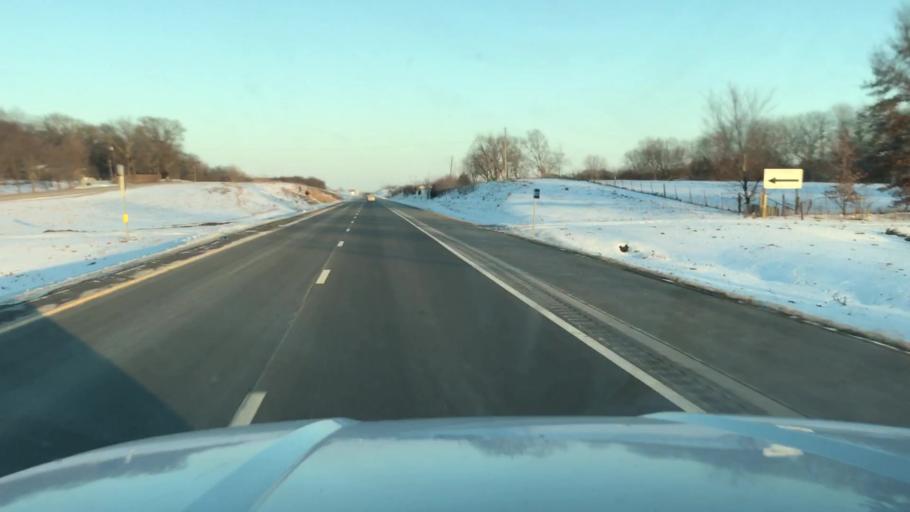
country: US
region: Missouri
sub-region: DeKalb County
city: Maysville
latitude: 39.7620
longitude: -94.4781
